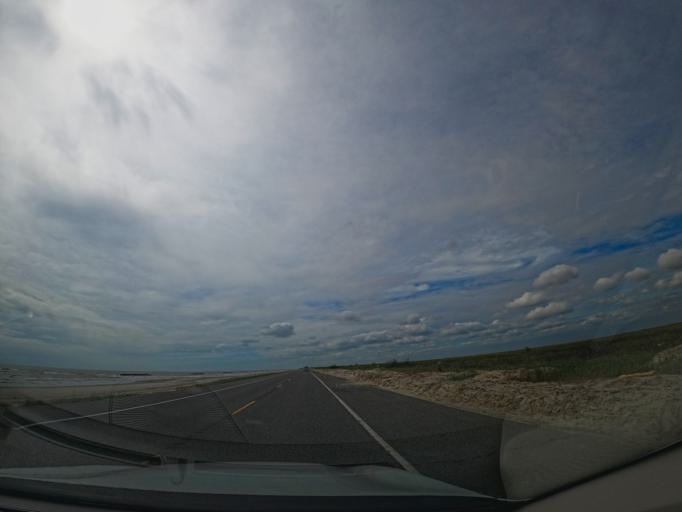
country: US
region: Louisiana
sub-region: Cameron Parish
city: Cameron
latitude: 29.7666
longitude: -93.5186
